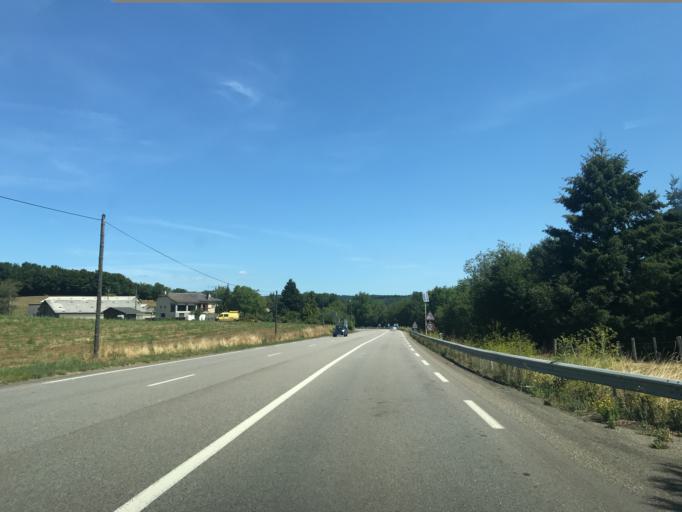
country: FR
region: Limousin
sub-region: Departement de la Correze
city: Tulle
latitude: 45.2887
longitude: 1.8038
